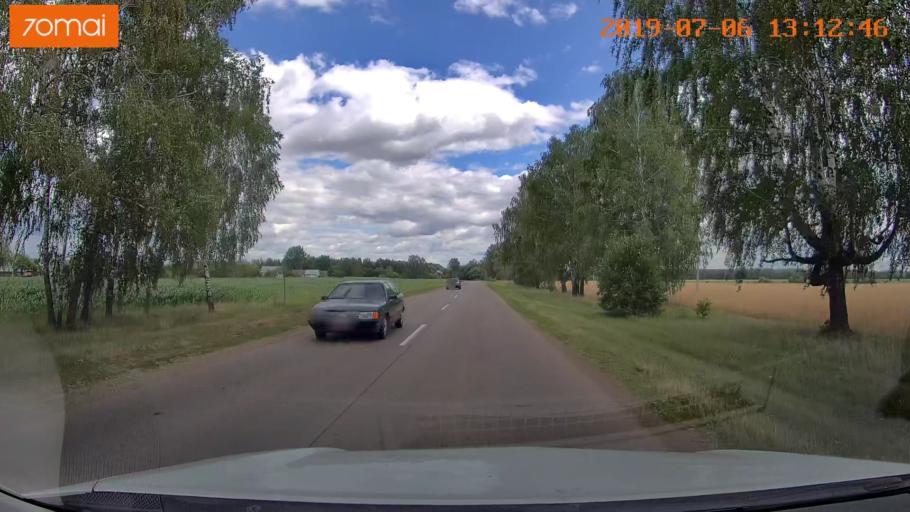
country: BY
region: Minsk
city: Enyerhyetykaw
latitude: 53.6582
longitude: 26.9952
